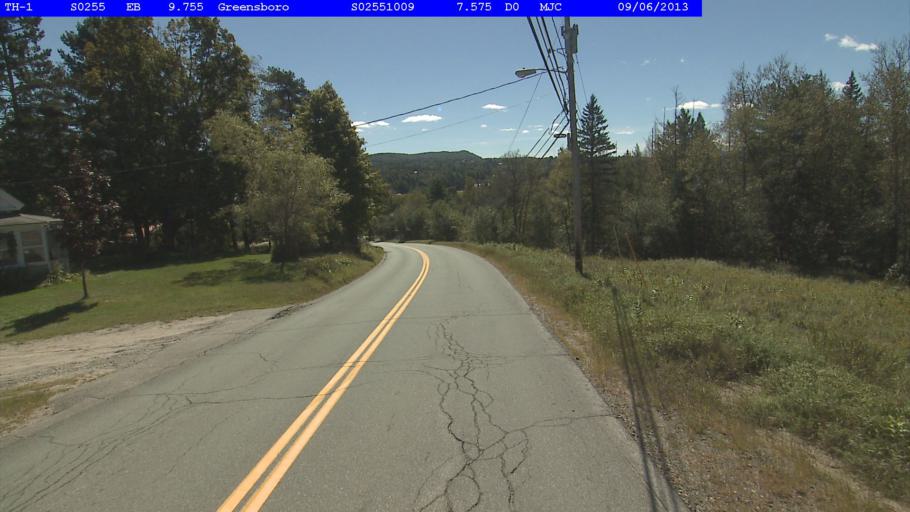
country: US
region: Vermont
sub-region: Caledonia County
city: Hardwick
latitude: 44.5500
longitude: -72.2658
